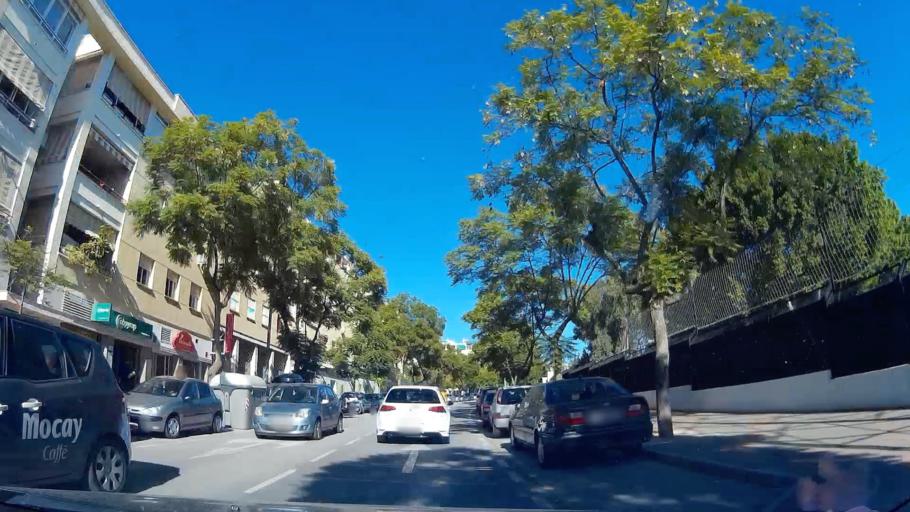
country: ES
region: Andalusia
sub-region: Provincia de Malaga
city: Malaga
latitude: 36.7190
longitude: -4.4760
